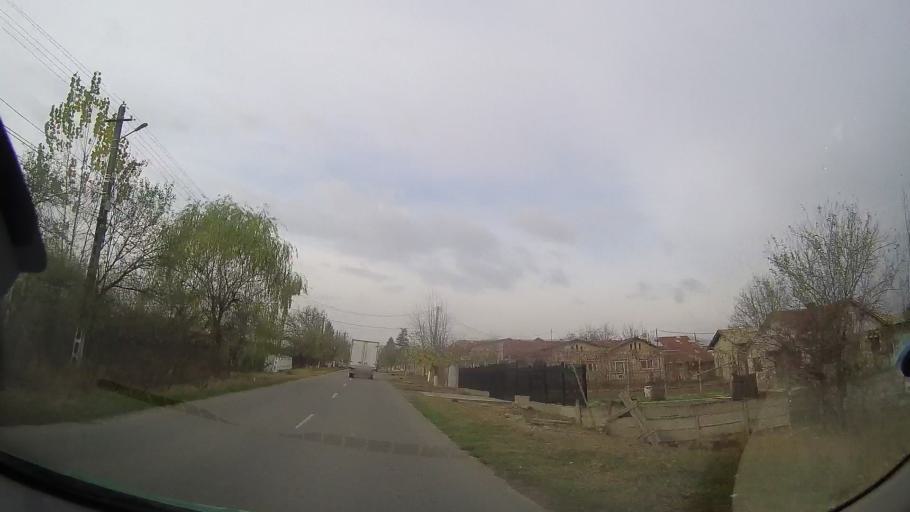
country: RO
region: Prahova
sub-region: Comuna Gorgota
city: Potigrafu
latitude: 44.7734
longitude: 26.1073
